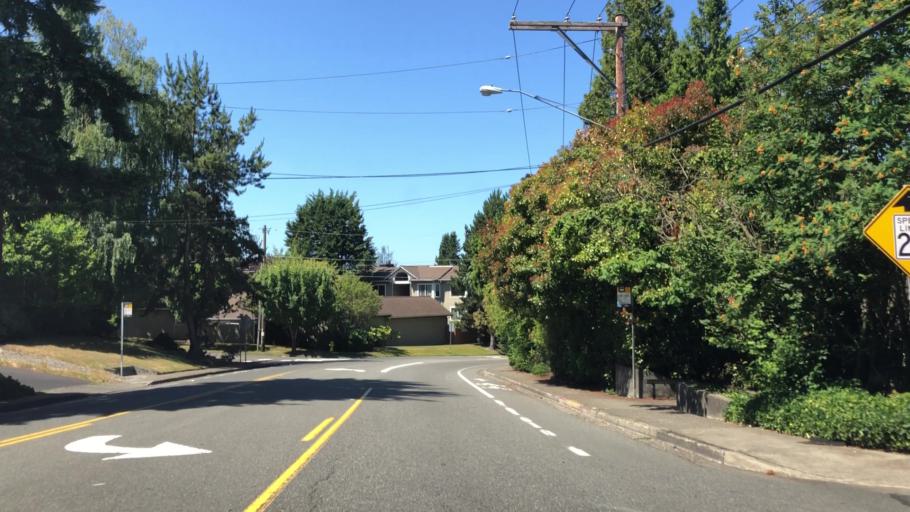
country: US
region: Washington
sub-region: King County
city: Kirkland
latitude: 47.6662
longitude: -122.1927
